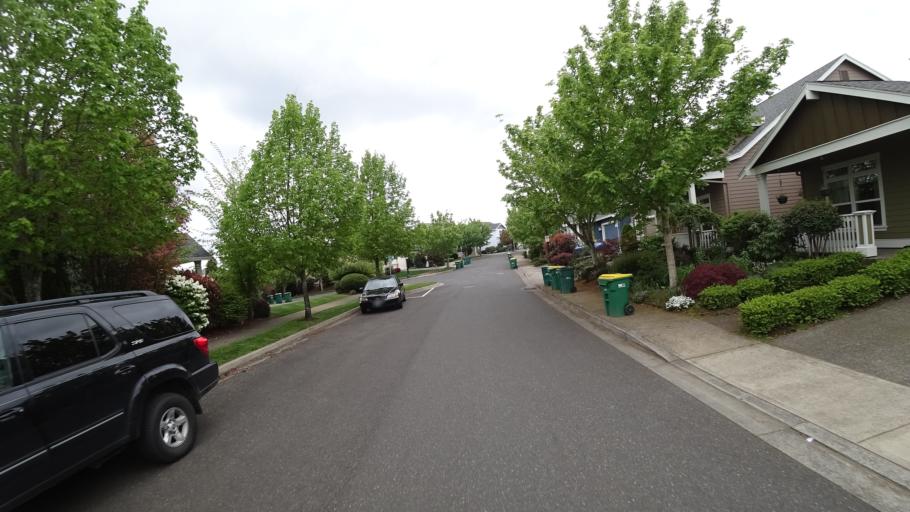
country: US
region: Oregon
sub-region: Washington County
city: Beaverton
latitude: 45.4578
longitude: -122.8289
